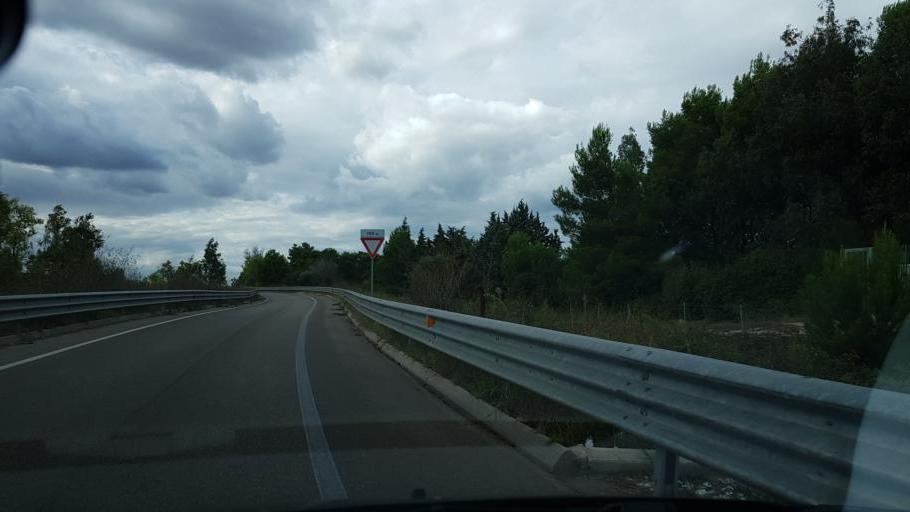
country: IT
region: Apulia
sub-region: Provincia di Lecce
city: Maglie
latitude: 40.1228
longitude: 18.3159
